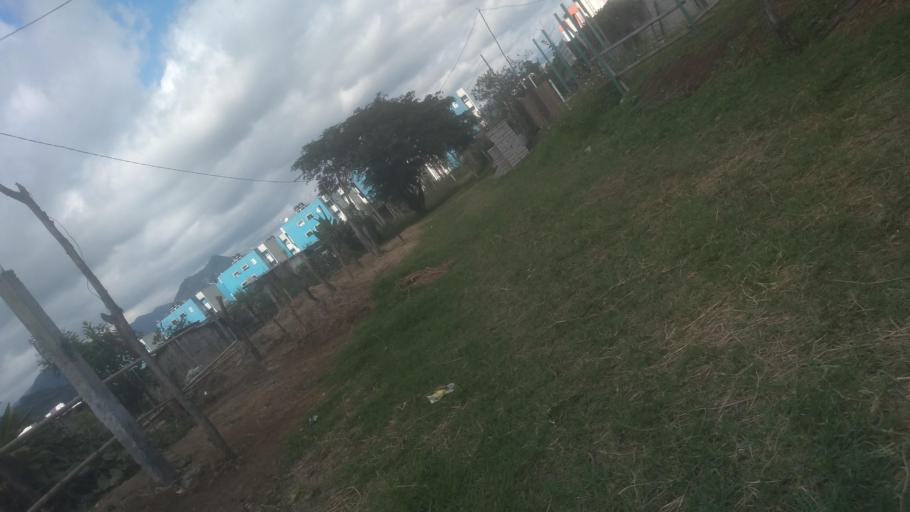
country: MX
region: Veracruz
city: Ixtac Zoquitlan
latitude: 18.8807
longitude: -97.0626
